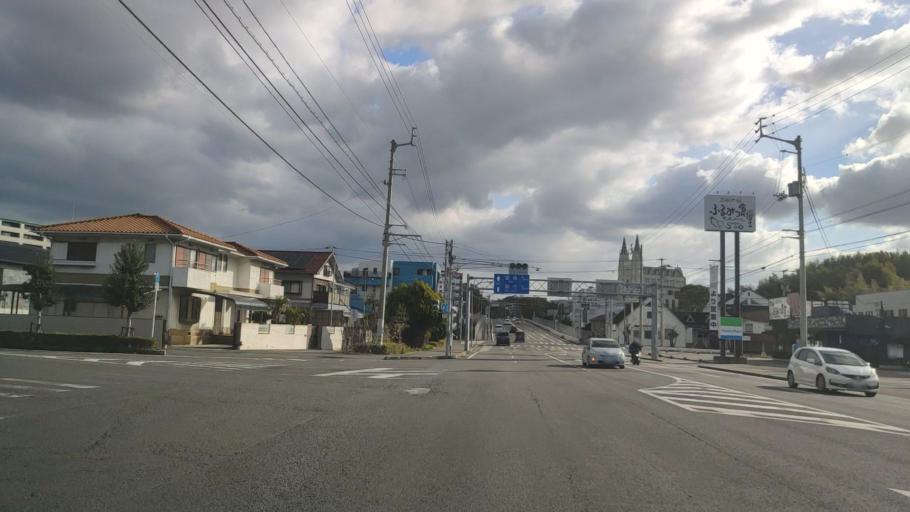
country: JP
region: Ehime
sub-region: Shikoku-chuo Shi
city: Matsuyama
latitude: 33.8569
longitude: 132.7257
